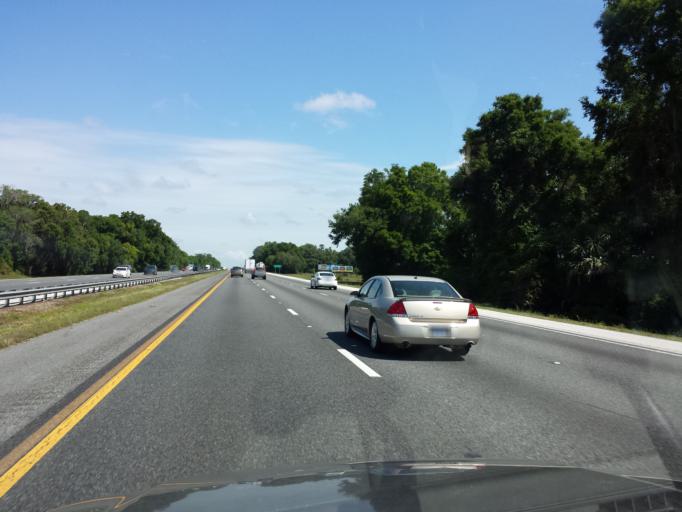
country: US
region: Florida
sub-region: Marion County
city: Ocala
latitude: 29.1078
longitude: -82.1848
